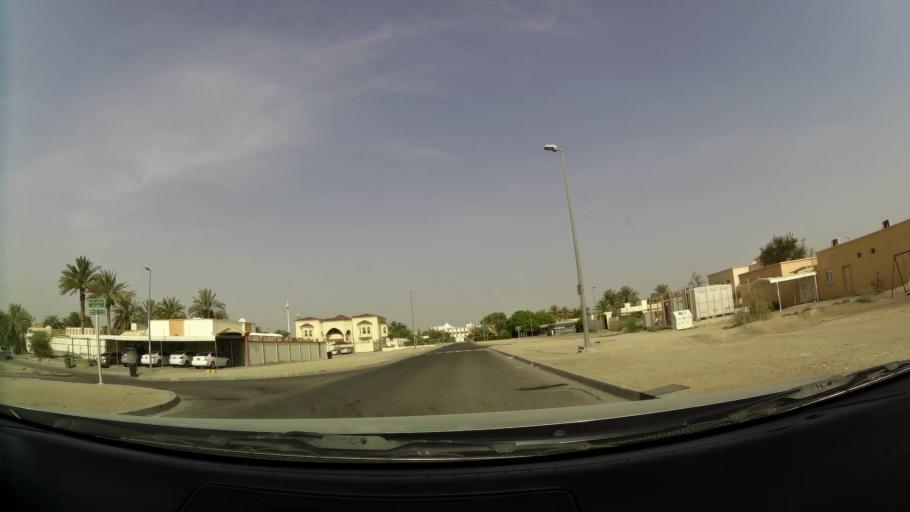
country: AE
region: Abu Dhabi
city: Al Ain
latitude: 24.1385
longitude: 55.7103
